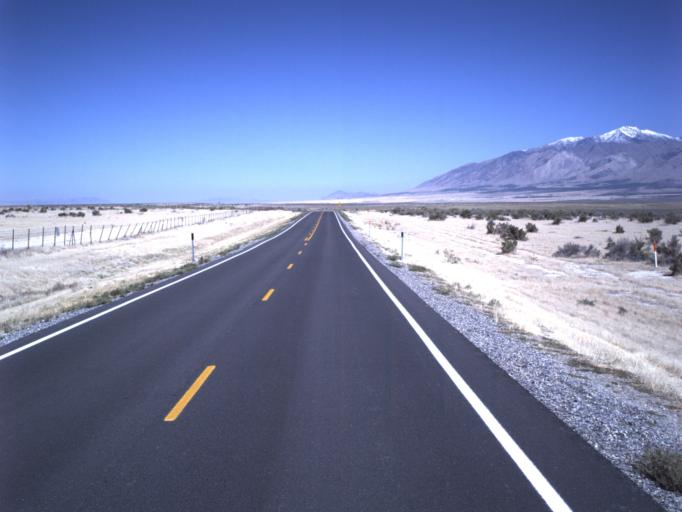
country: US
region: Utah
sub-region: Tooele County
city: Grantsville
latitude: 40.2398
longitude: -112.7232
